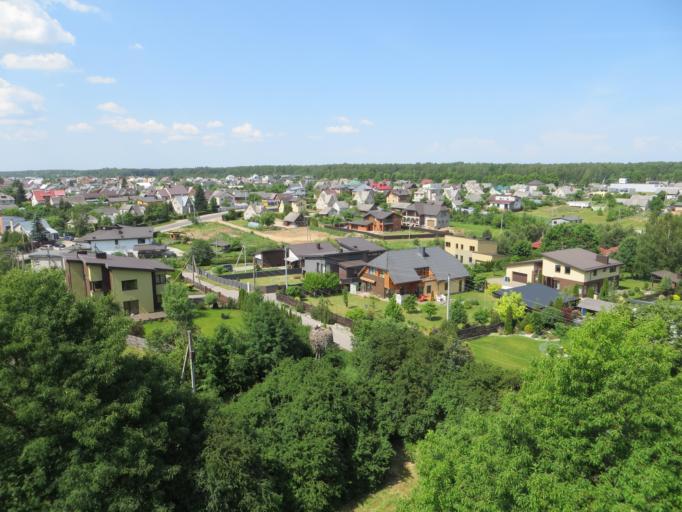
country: LT
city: Ramuciai
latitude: 54.9510
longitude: 24.0377
